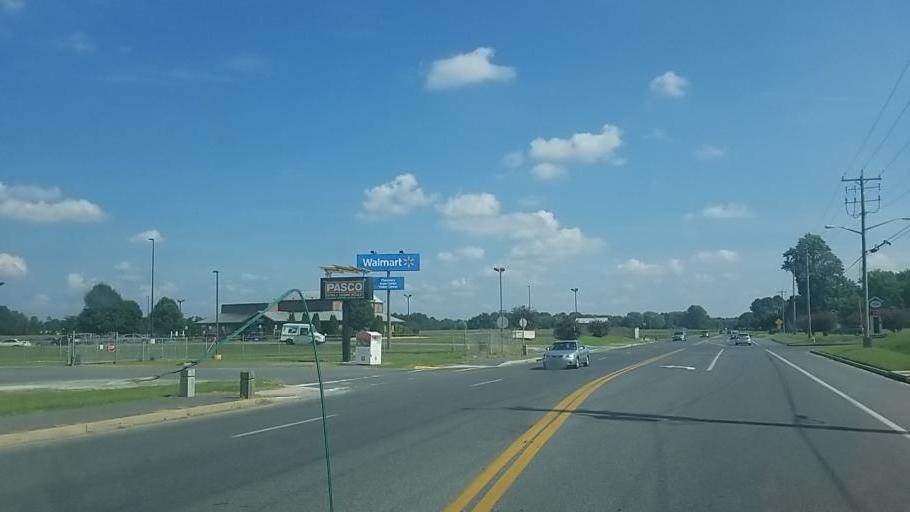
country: US
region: Maryland
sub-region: Wicomico County
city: Fruitland
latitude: 38.3276
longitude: -75.6137
